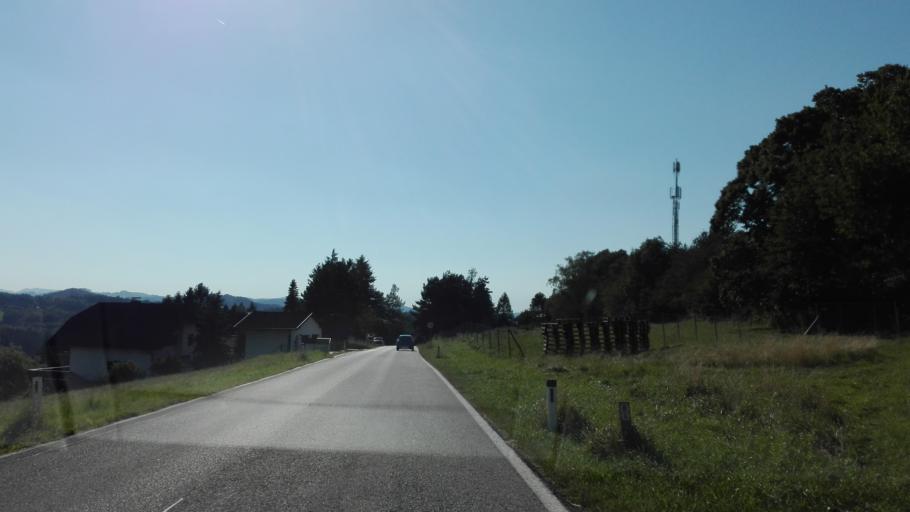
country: AT
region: Lower Austria
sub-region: Politischer Bezirk Sankt Polten
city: Eichgraben
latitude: 48.1488
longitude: 15.9762
